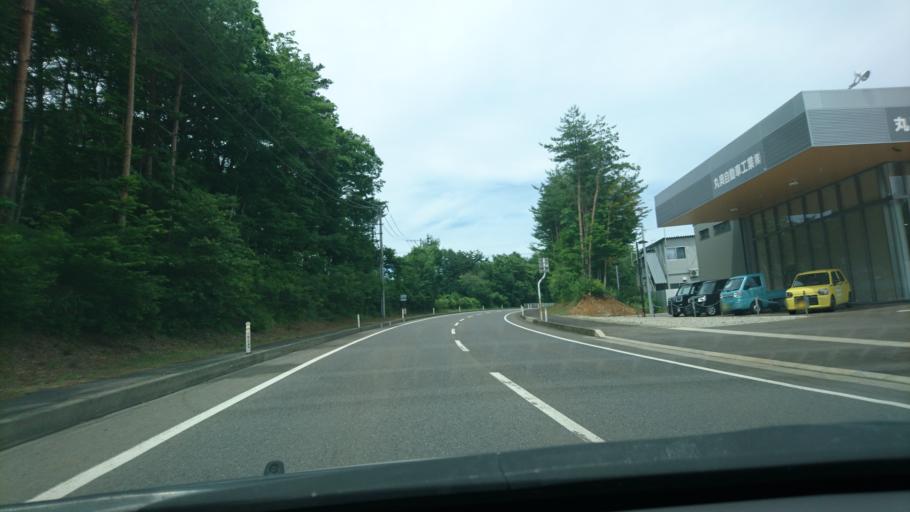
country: JP
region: Iwate
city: Miyako
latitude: 39.9116
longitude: 141.9023
